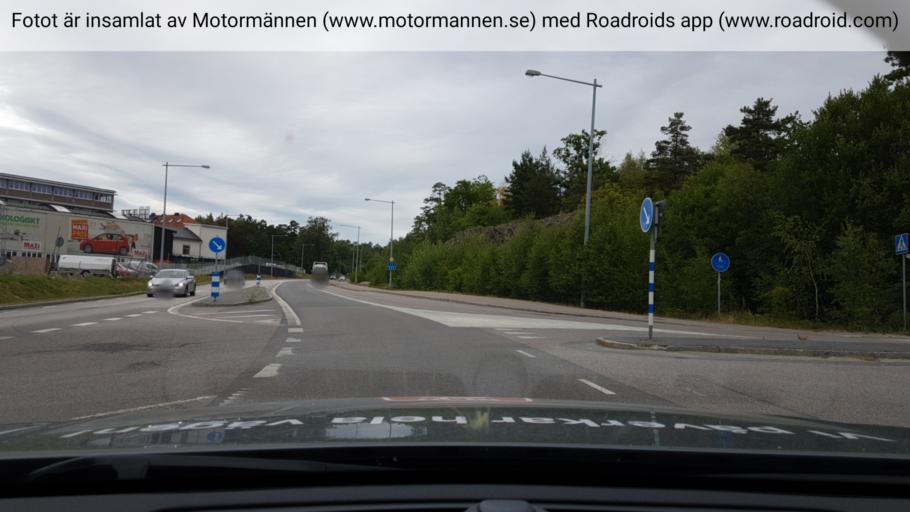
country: SE
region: Stockholm
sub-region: Nynashamns Kommun
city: Nynashamn
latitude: 58.9120
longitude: 17.9578
